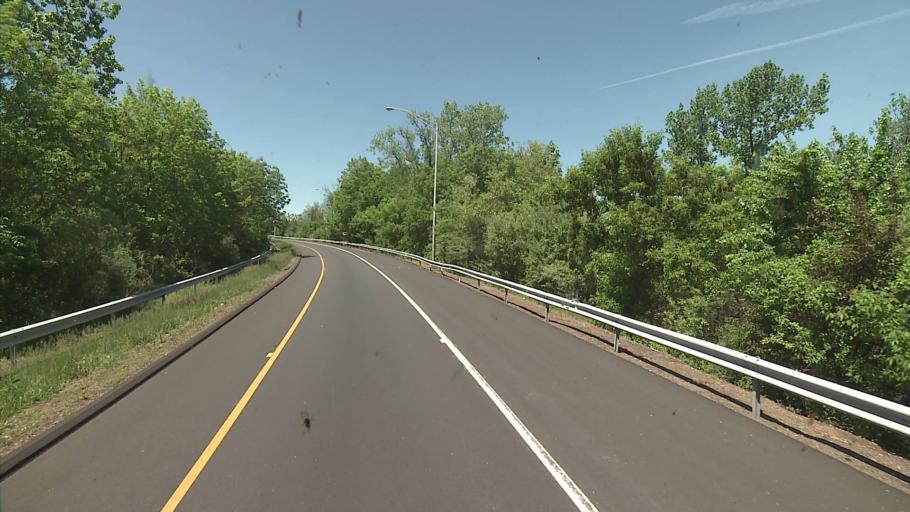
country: US
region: Connecticut
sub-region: Hartford County
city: West Hartford
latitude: 41.7280
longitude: -72.7691
